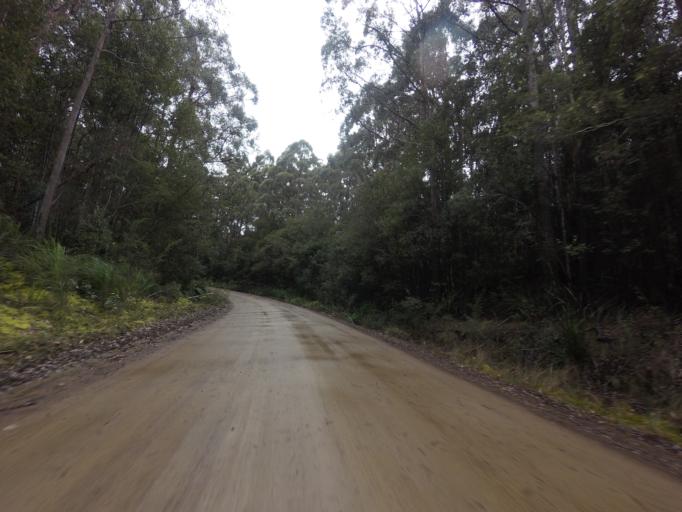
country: AU
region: Tasmania
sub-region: Huon Valley
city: Geeveston
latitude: -43.4993
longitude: 146.8790
